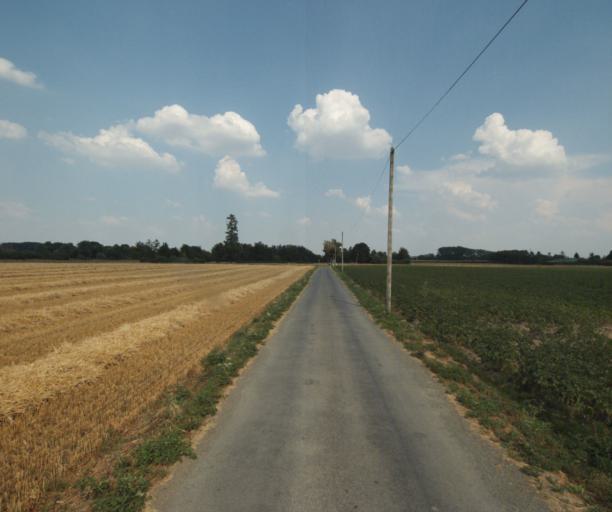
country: FR
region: Nord-Pas-de-Calais
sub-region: Departement du Nord
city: Linselles
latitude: 50.7225
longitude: 3.0549
